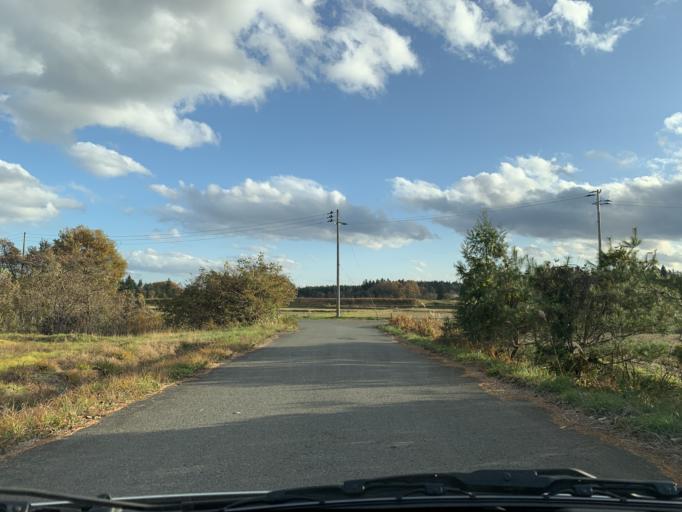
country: JP
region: Iwate
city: Mizusawa
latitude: 39.1198
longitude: 140.9942
